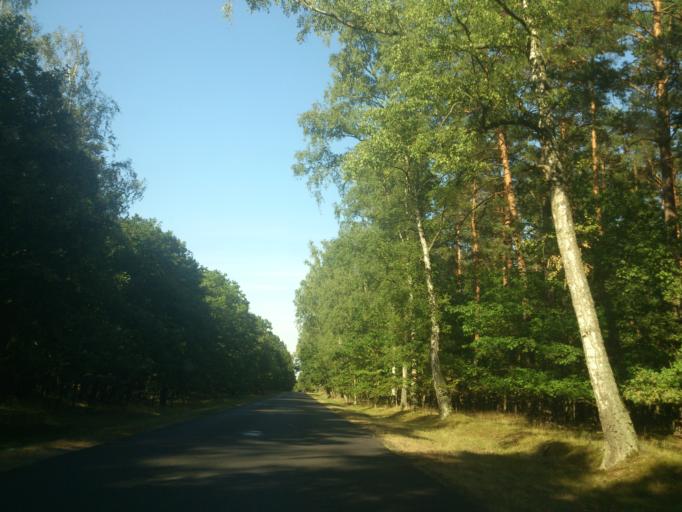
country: PL
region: Kujawsko-Pomorskie
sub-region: Powiat golubsko-dobrzynski
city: Ciechocin
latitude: 53.0853
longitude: 18.9831
